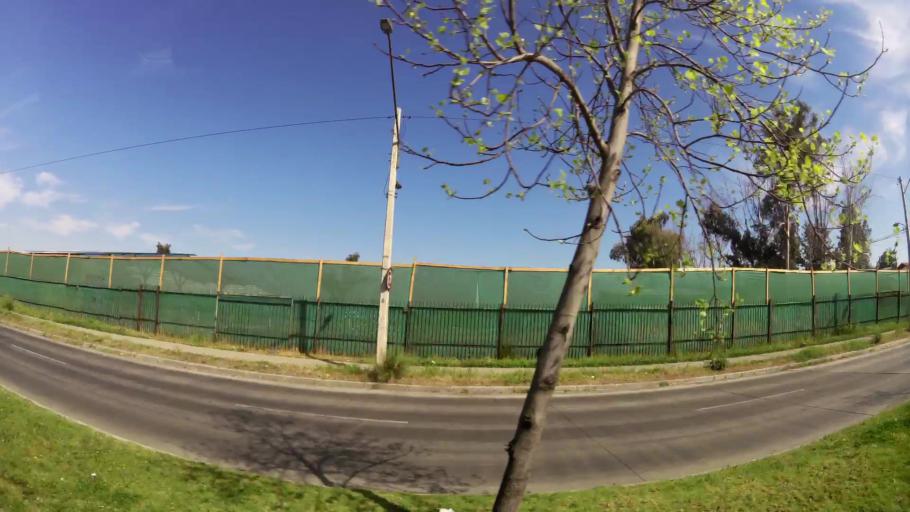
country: CL
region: Santiago Metropolitan
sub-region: Provincia de Santiago
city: Villa Presidente Frei, Nunoa, Santiago, Chile
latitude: -33.4503
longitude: -70.5400
